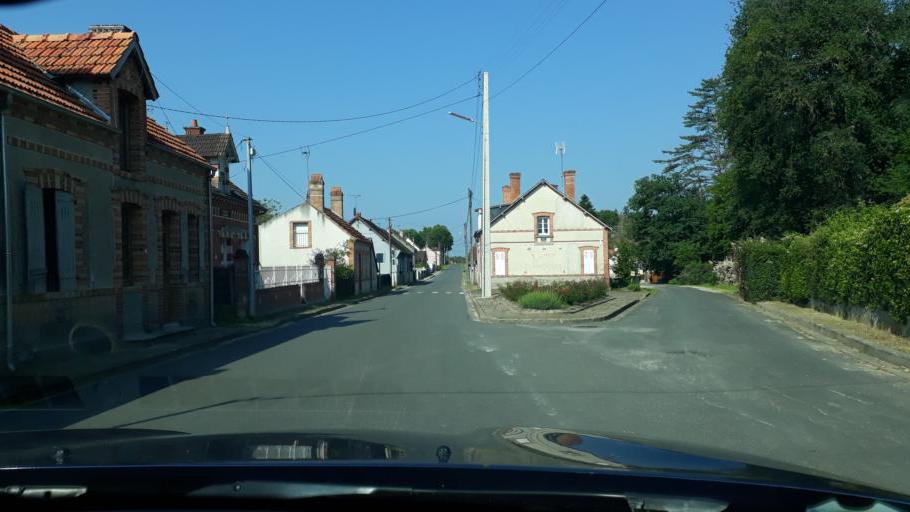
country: FR
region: Centre
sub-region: Departement du Loiret
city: Ligny-le-Ribault
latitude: 47.6227
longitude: 1.7528
